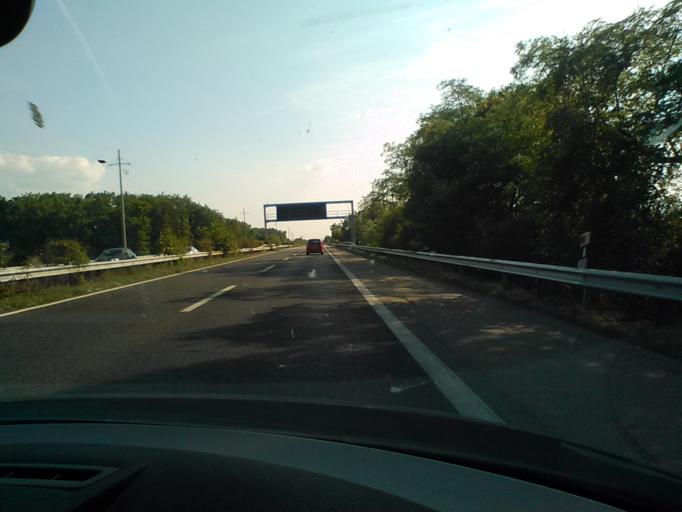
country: CH
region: Geneva
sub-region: Geneva
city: Bellevue
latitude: 46.2717
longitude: 6.1383
